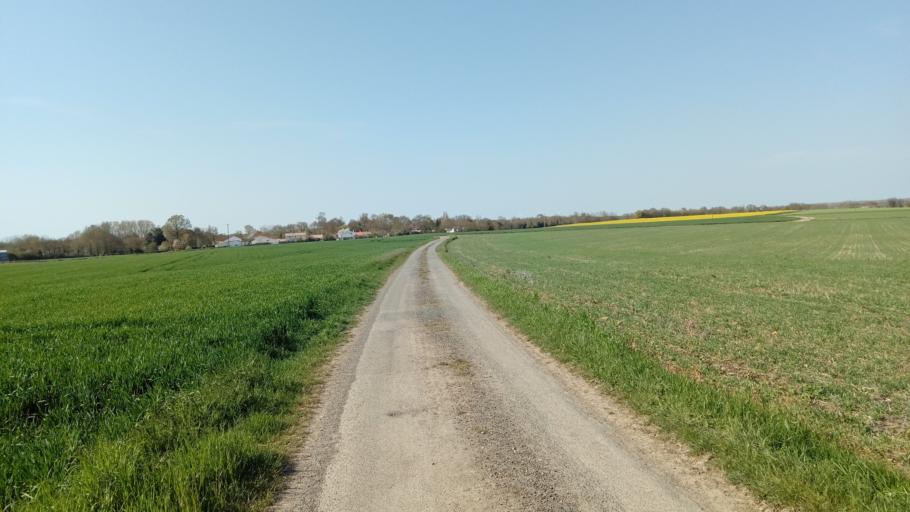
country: FR
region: Poitou-Charentes
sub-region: Departement de la Charente-Maritime
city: Verines
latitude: 46.1633
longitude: -0.9407
